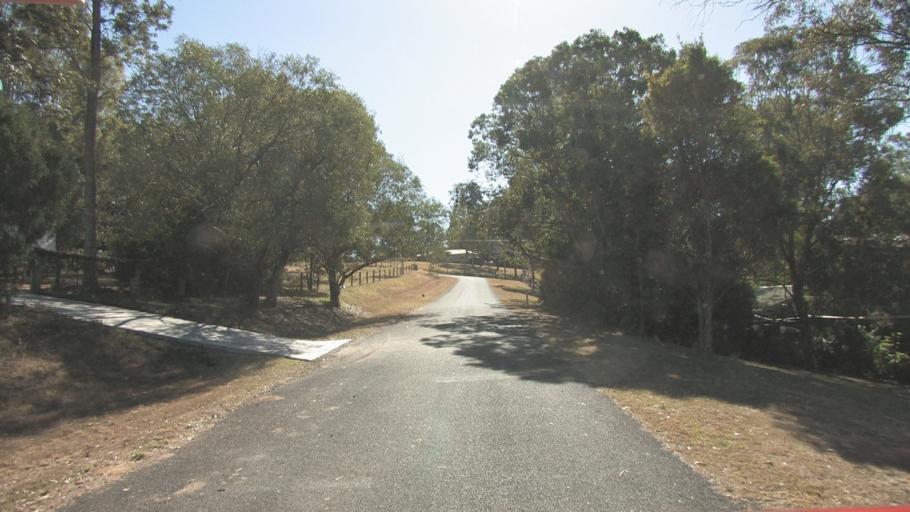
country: AU
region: Queensland
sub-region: Logan
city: Cedar Vale
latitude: -27.8940
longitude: 152.9787
